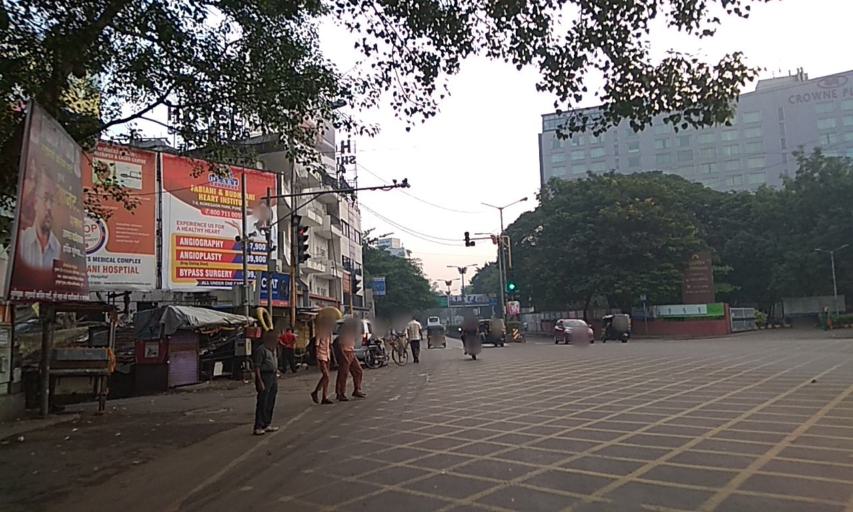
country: IN
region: Maharashtra
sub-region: Pune Division
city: Shivaji Nagar
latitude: 18.5307
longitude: 73.8754
